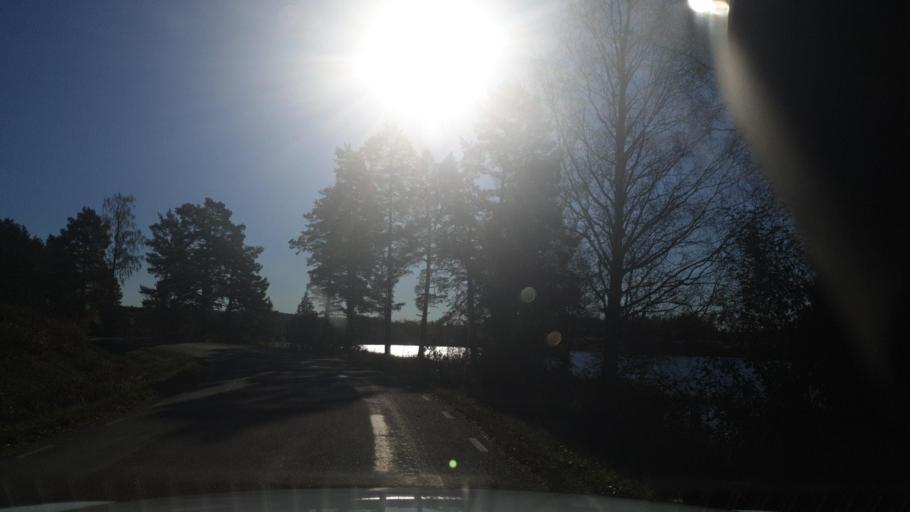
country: SE
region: Vaermland
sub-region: Arvika Kommun
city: Arvika
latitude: 59.5398
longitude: 12.7802
